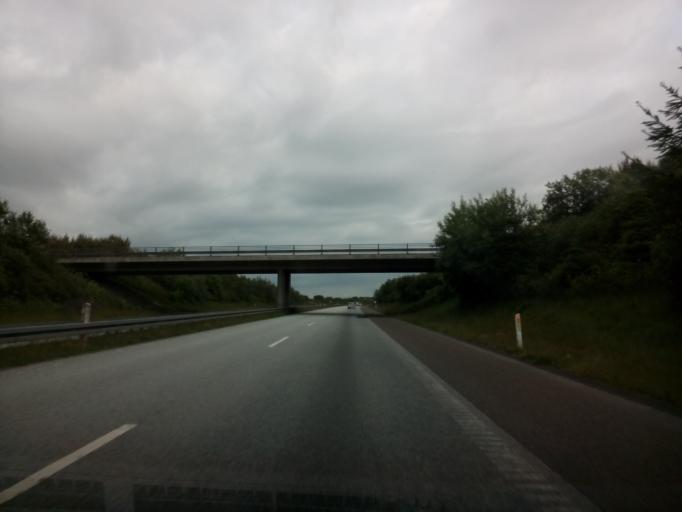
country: DK
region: North Denmark
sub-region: Hjorring Kommune
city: Vra
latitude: 57.3633
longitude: 10.0256
